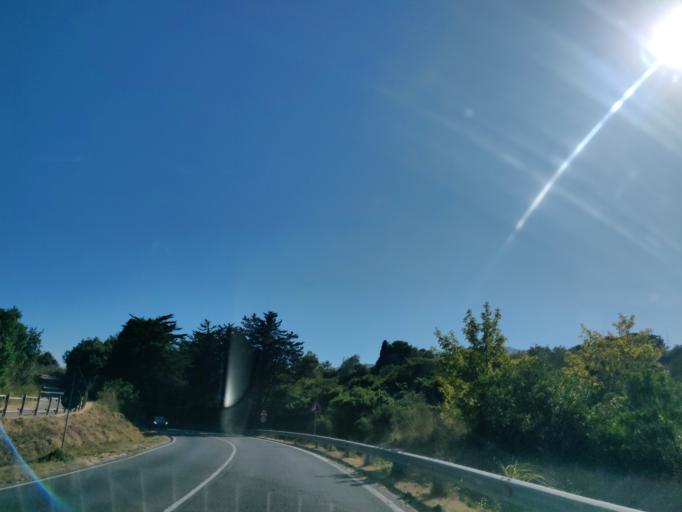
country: IT
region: Tuscany
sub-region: Provincia di Grosseto
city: Porto Ercole
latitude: 42.4089
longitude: 11.2007
